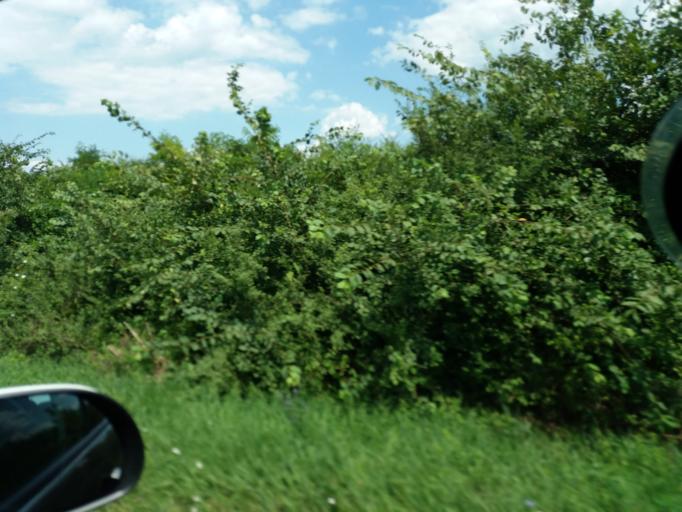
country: RS
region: Autonomna Pokrajina Vojvodina
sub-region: Sremski Okrug
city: Pecinci
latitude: 44.8710
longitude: 19.9626
